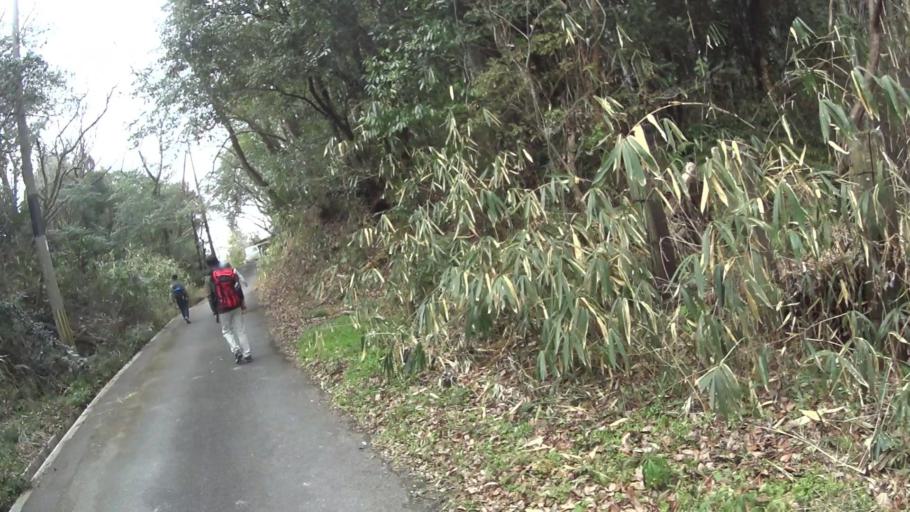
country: JP
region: Nara
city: Nara-shi
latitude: 34.7332
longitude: 135.8515
